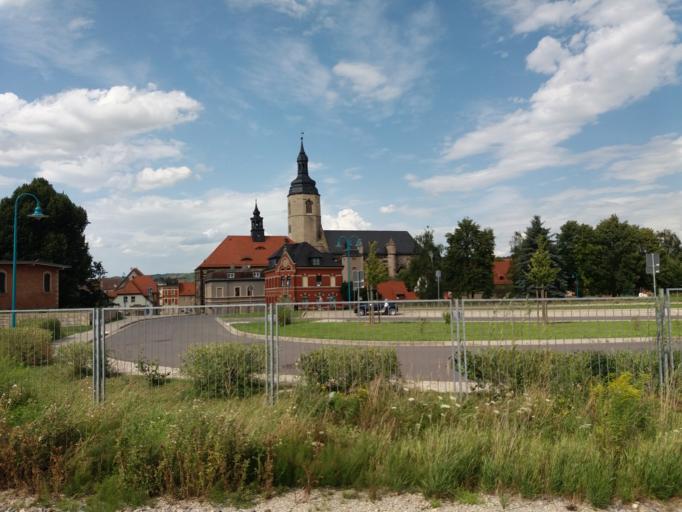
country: DE
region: Saxony-Anhalt
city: Laucha
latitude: 51.2219
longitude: 11.6793
